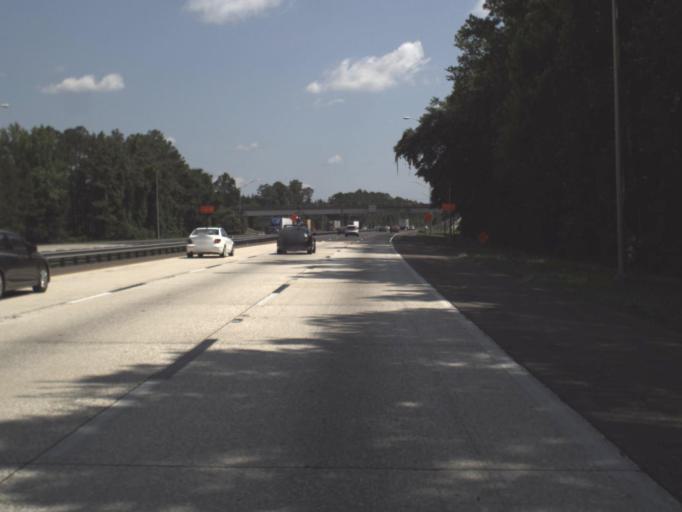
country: US
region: Florida
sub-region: Nassau County
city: Yulee
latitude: 30.4882
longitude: -81.6421
